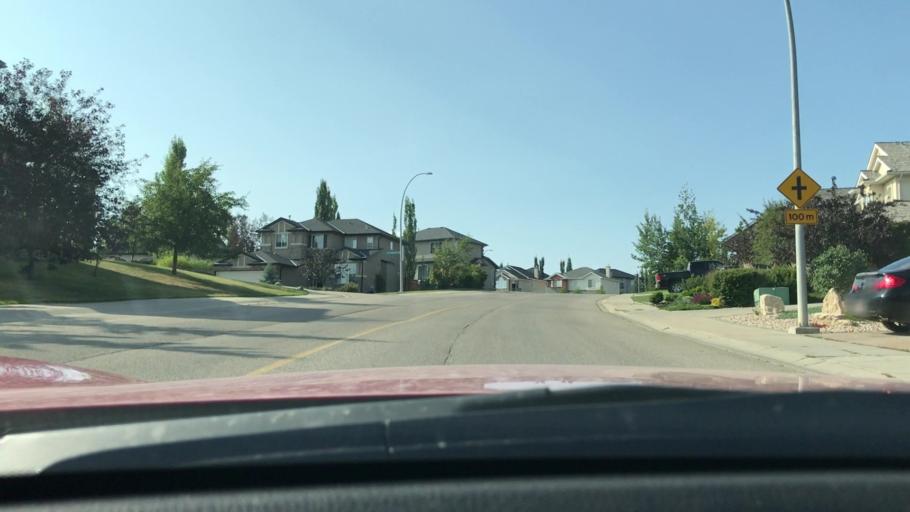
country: CA
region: Alberta
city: Calgary
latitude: 51.0280
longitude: -114.1819
